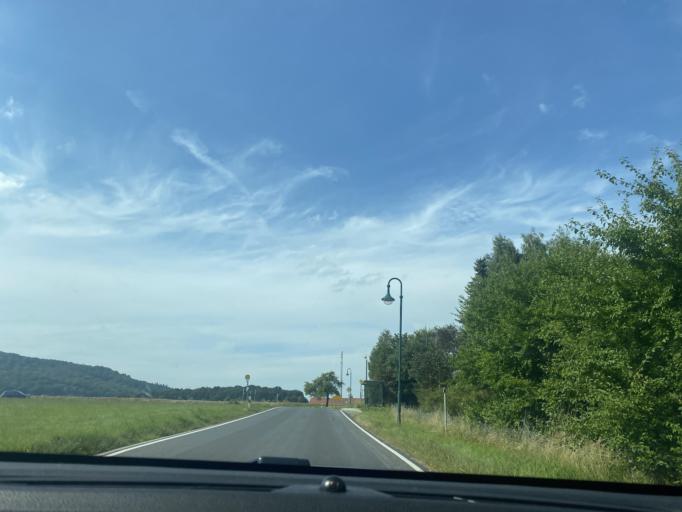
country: DE
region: Saxony
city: Sohland am Rotstein
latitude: 51.0973
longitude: 14.7904
